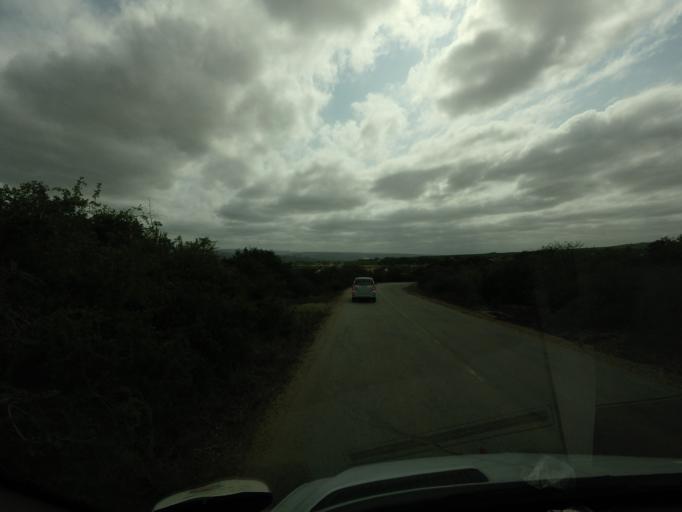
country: ZA
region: Eastern Cape
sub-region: Cacadu District Municipality
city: Kirkwood
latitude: -33.4443
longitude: 25.7408
